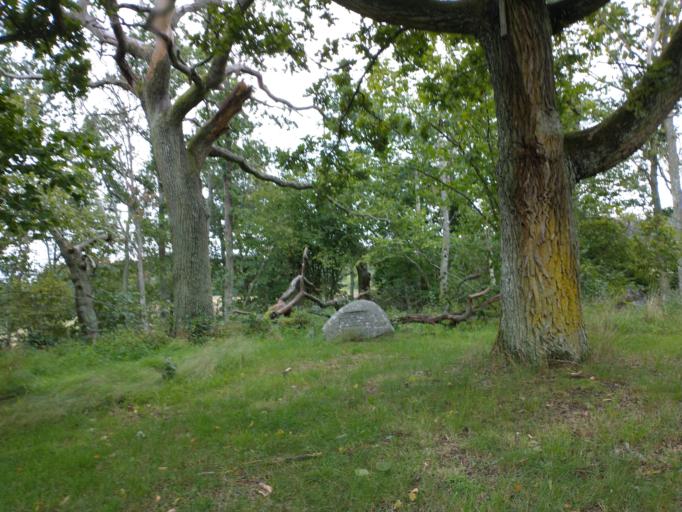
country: SE
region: Kalmar
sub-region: Kalmar Kommun
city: Lindsdal
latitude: 56.7798
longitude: 16.2932
